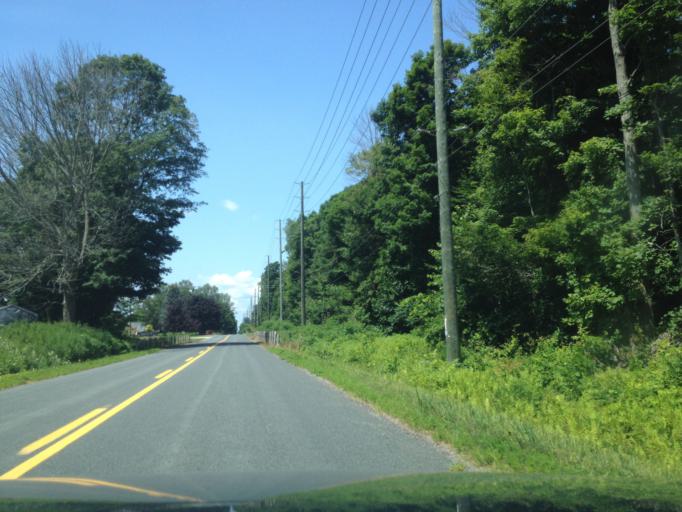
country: CA
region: Ontario
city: Aylmer
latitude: 42.6502
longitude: -80.7663
